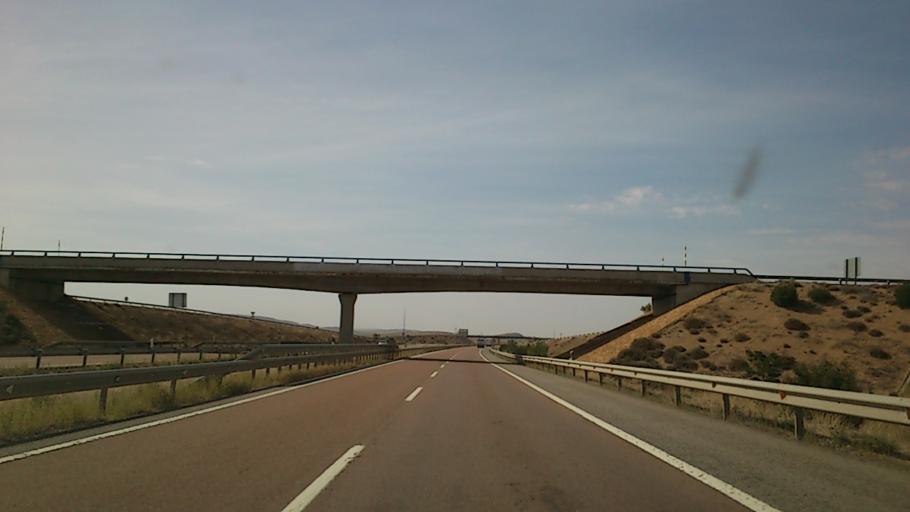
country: ES
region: Aragon
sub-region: Provincia de Teruel
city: Singra
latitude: 40.6211
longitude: -1.2968
